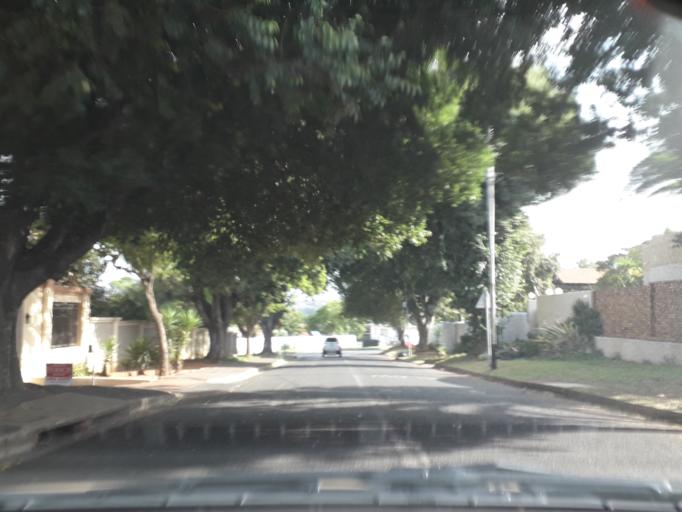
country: ZA
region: Gauteng
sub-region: City of Johannesburg Metropolitan Municipality
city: Johannesburg
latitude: -26.1759
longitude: 28.0975
